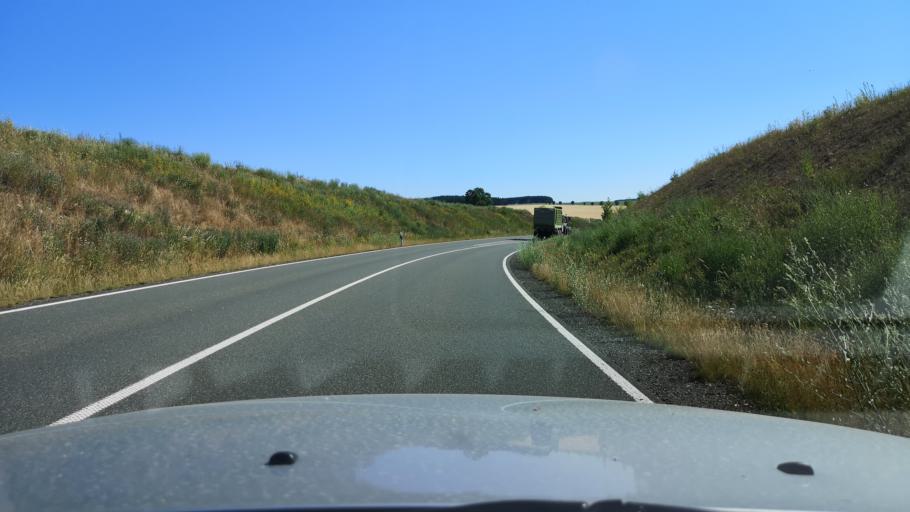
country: DE
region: Thuringia
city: Birkenhugel
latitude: 50.4429
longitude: 11.7546
